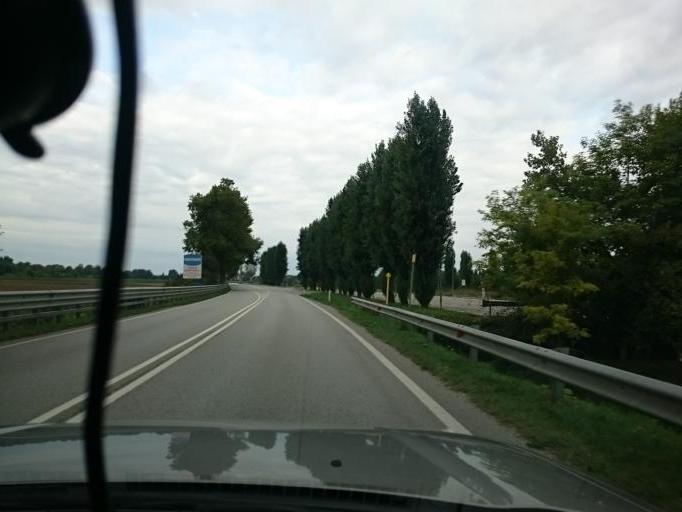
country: IT
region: Veneto
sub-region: Provincia di Padova
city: Arlesega
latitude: 45.4534
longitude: 11.7256
